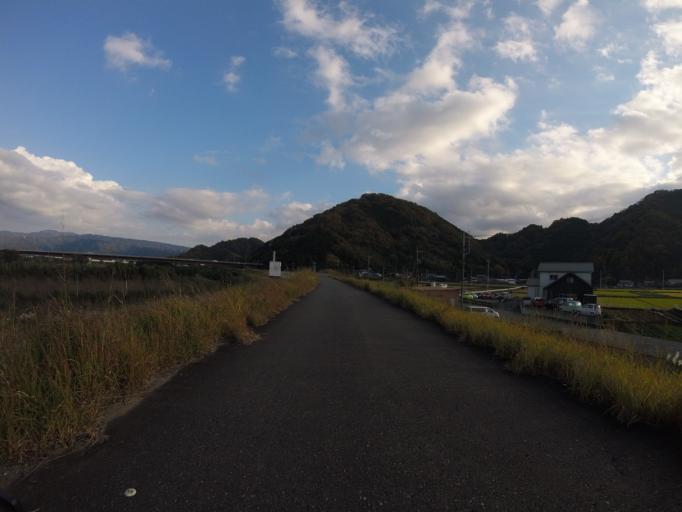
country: JP
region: Shizuoka
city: Mishima
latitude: 35.0693
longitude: 138.9212
